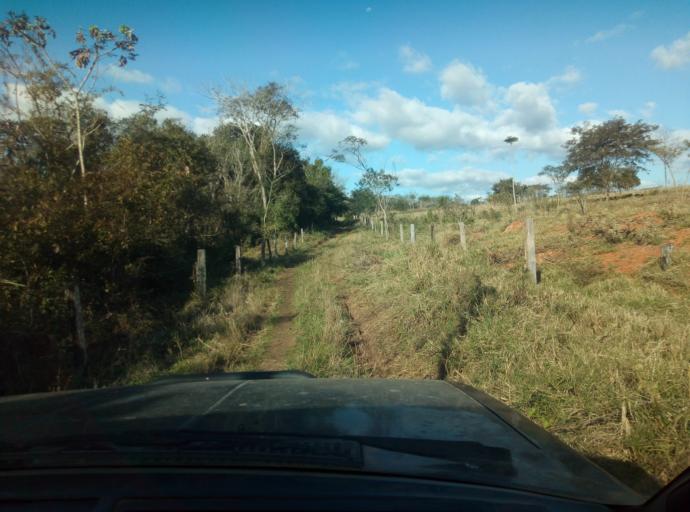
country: PY
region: Caaguazu
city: Carayao
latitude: -25.1744
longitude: -56.2720
